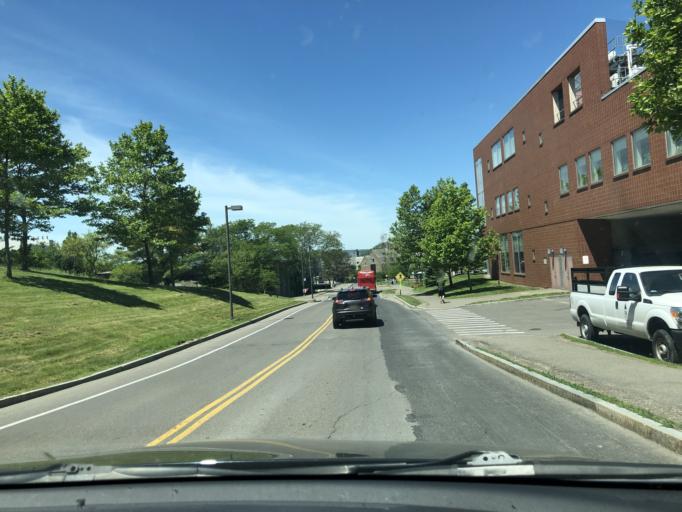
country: US
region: New York
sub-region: Tompkins County
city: Cayuga Heights
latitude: 42.4533
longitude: -76.4757
